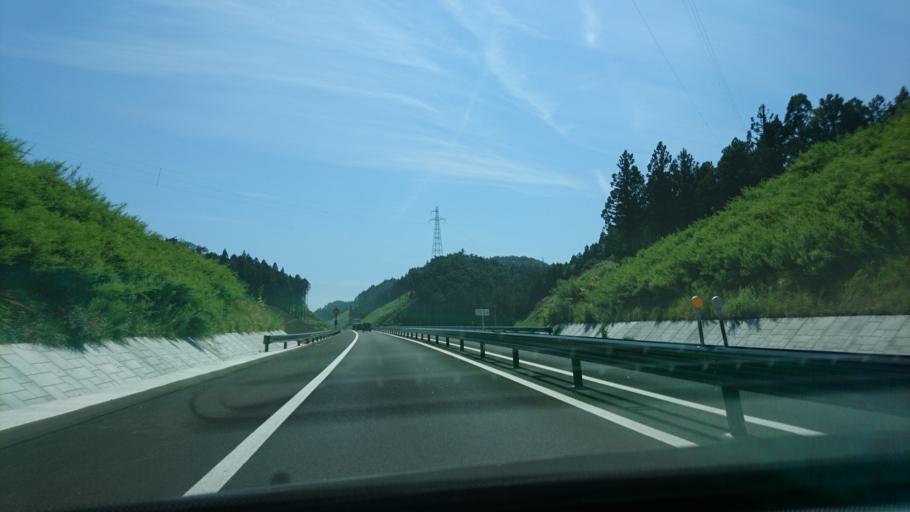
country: JP
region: Iwate
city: Ofunato
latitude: 39.0163
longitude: 141.6083
